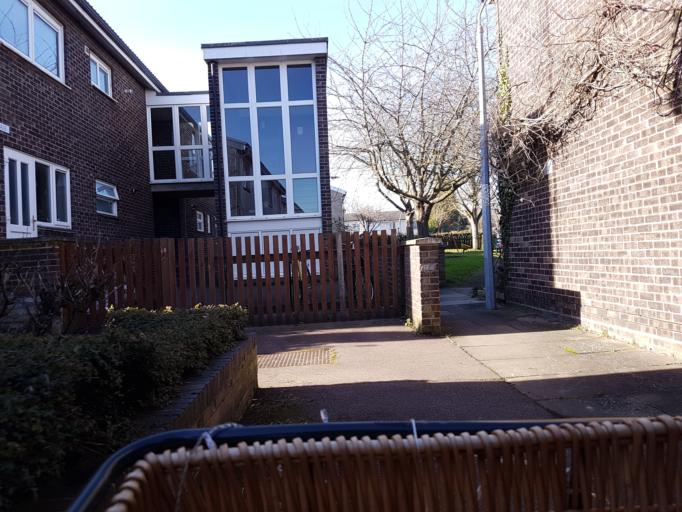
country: GB
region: England
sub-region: Cambridgeshire
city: Fulbourn
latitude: 52.1829
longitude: 0.1745
